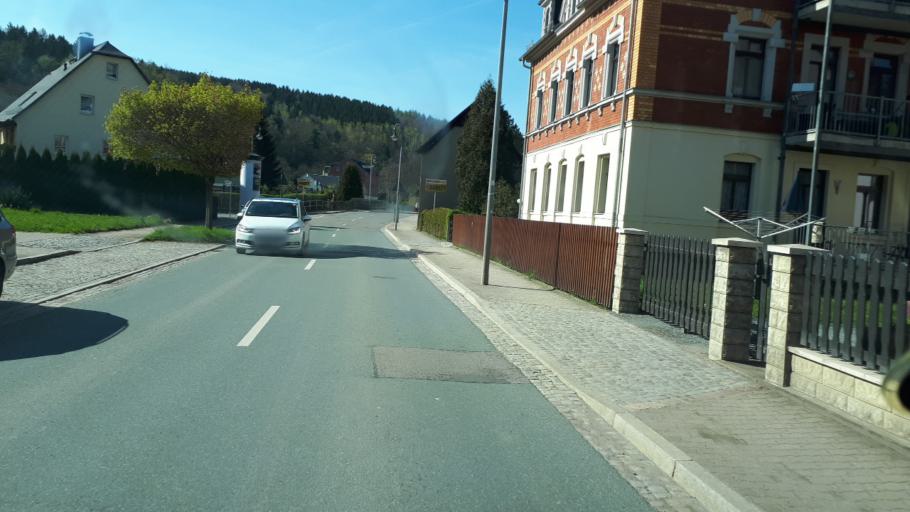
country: DE
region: Saxony
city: Gelenau
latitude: 50.7740
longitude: 12.9736
